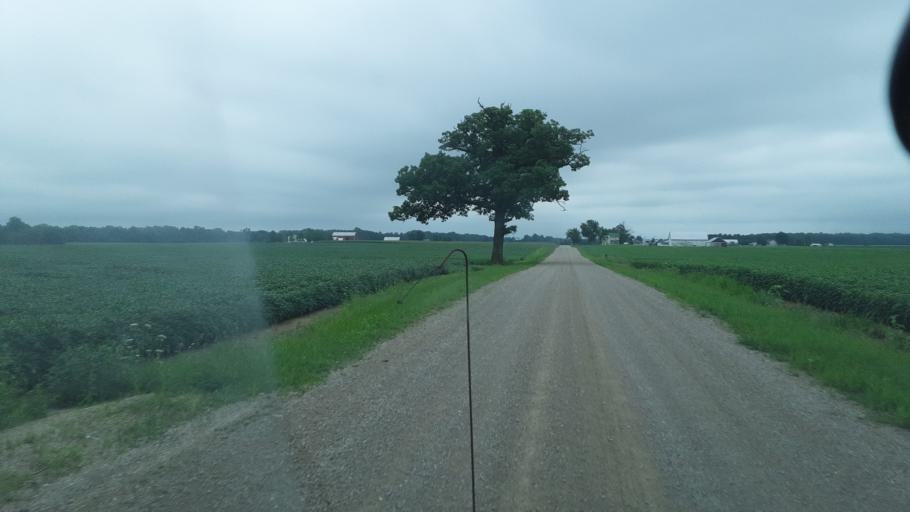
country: US
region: Indiana
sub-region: Adams County
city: Geneva
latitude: 40.6202
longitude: -85.0046
